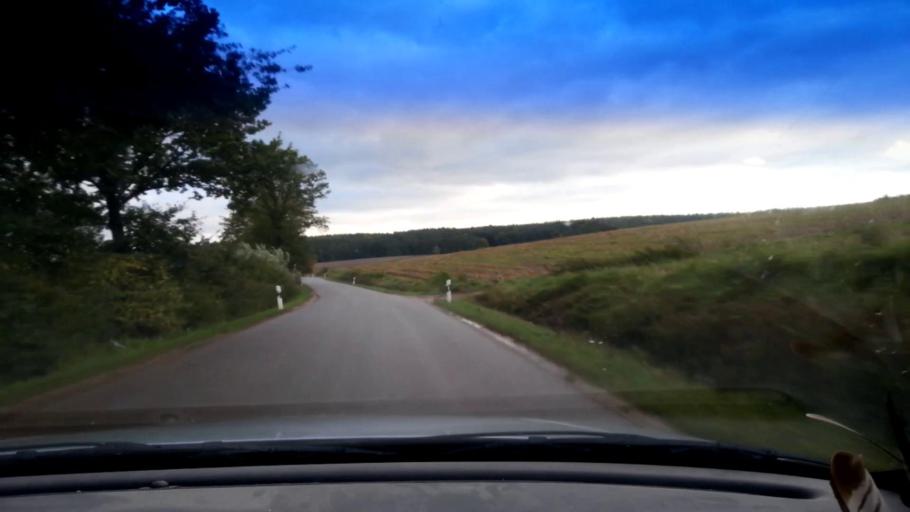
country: DE
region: Bavaria
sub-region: Upper Franconia
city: Burgebrach
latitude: 49.8126
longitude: 10.6906
